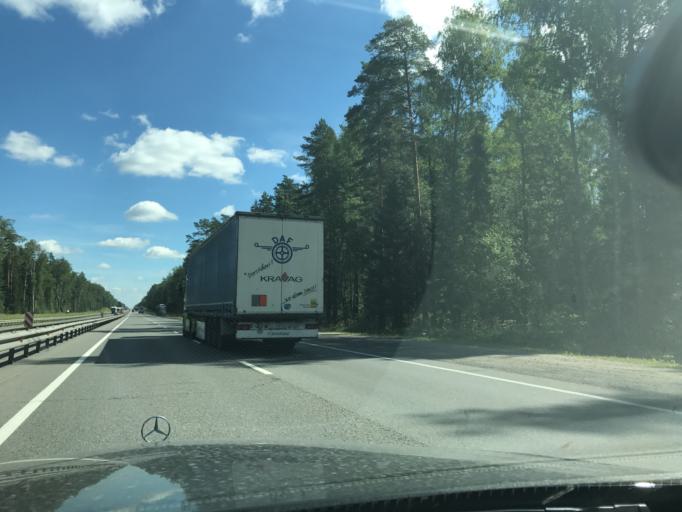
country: RU
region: Vladimir
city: Stepantsevo
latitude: 56.2218
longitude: 41.5365
